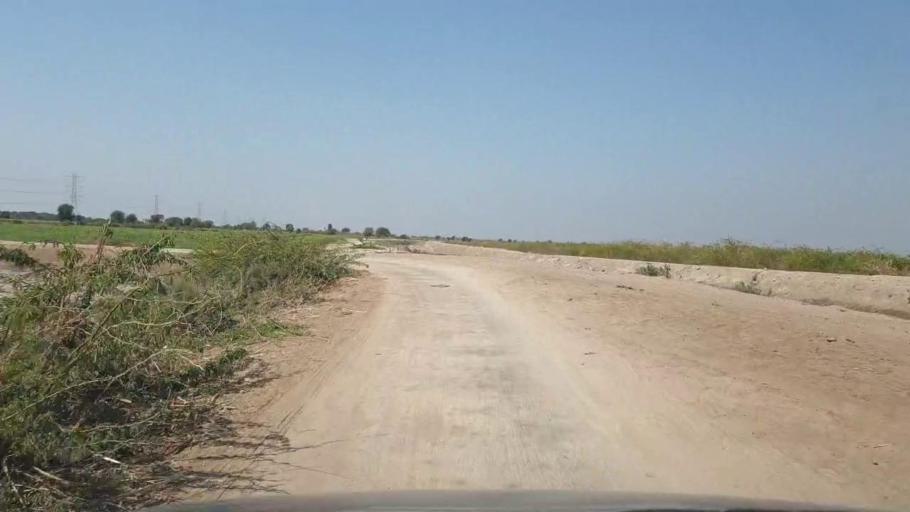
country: PK
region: Sindh
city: Digri
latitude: 25.1879
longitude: 69.2191
